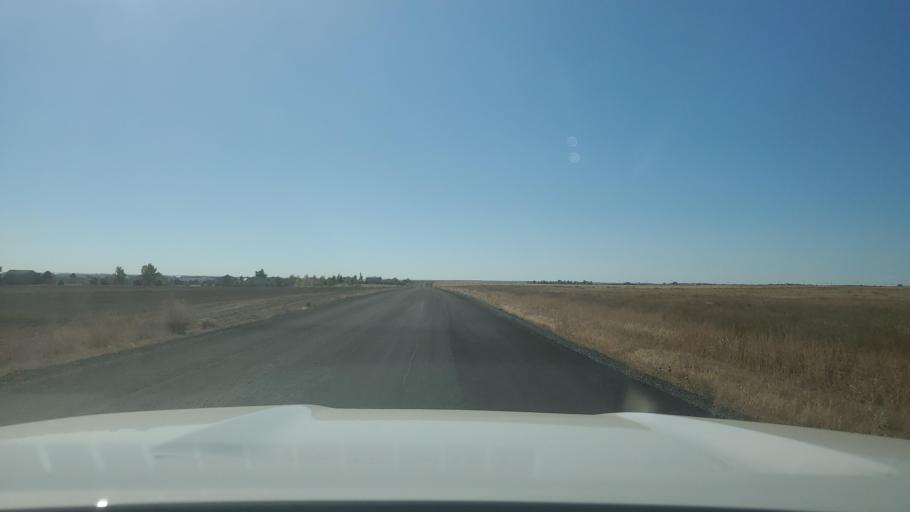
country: US
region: Colorado
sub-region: Adams County
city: Bennett
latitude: 39.7490
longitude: -104.3773
